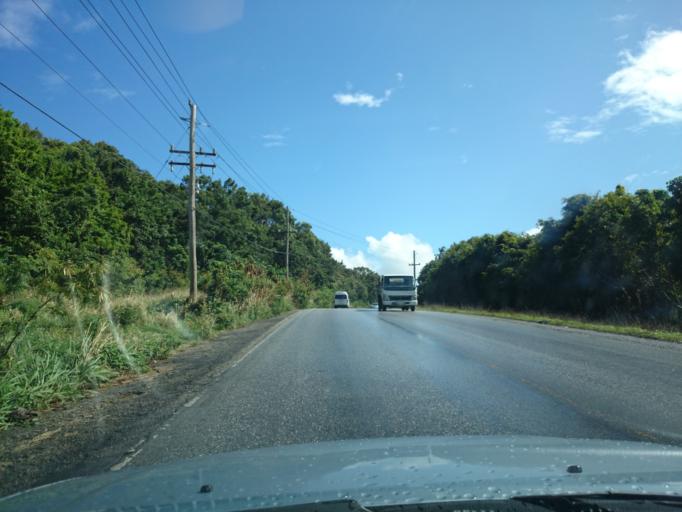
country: BB
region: Saint James
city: Holetown
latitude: 13.1986
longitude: -59.6139
